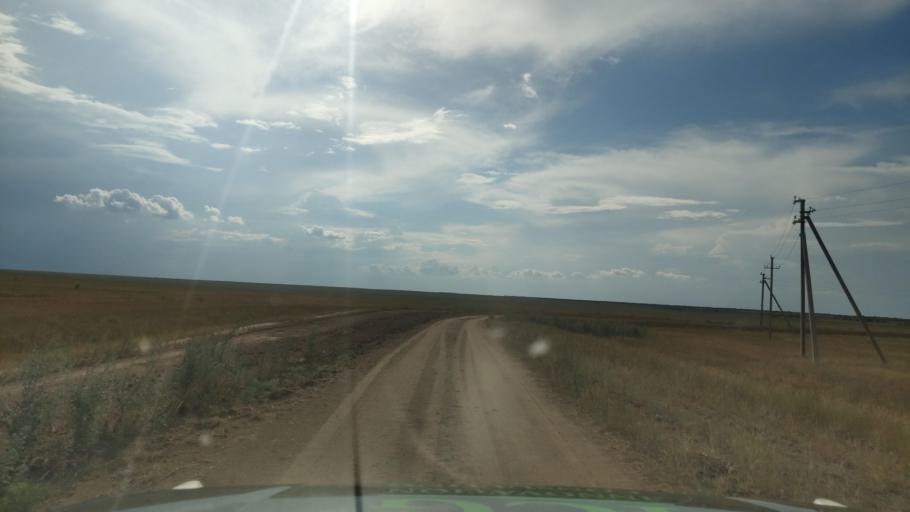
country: KZ
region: Pavlodar
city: Pavlodar
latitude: 52.5088
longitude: 77.5548
